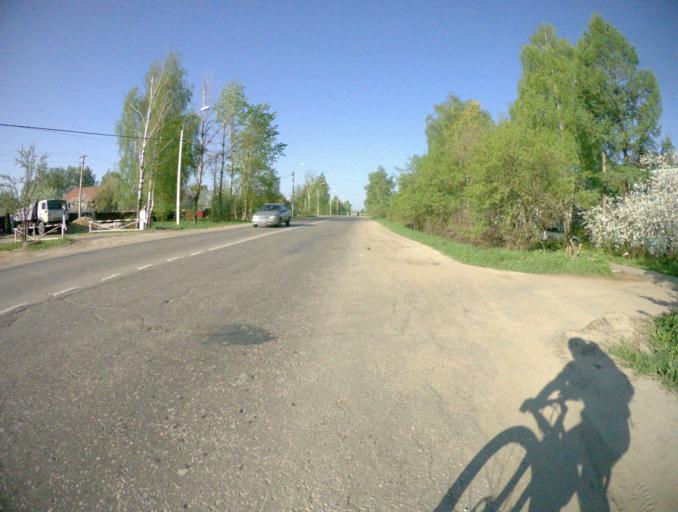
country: RU
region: Vladimir
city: Novovyazniki
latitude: 56.2109
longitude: 42.1696
